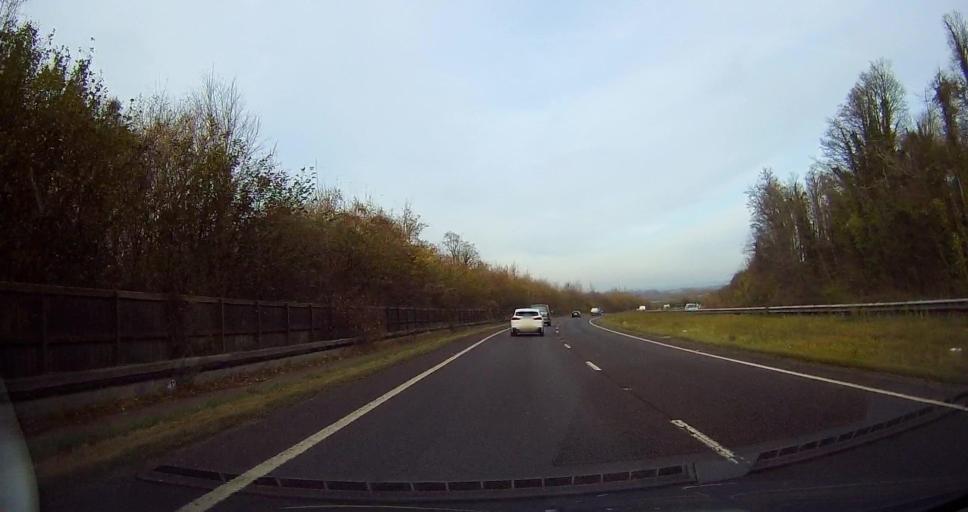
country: GB
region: England
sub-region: West Sussex
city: Hurstpierpoint
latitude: 50.9107
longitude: -0.1922
